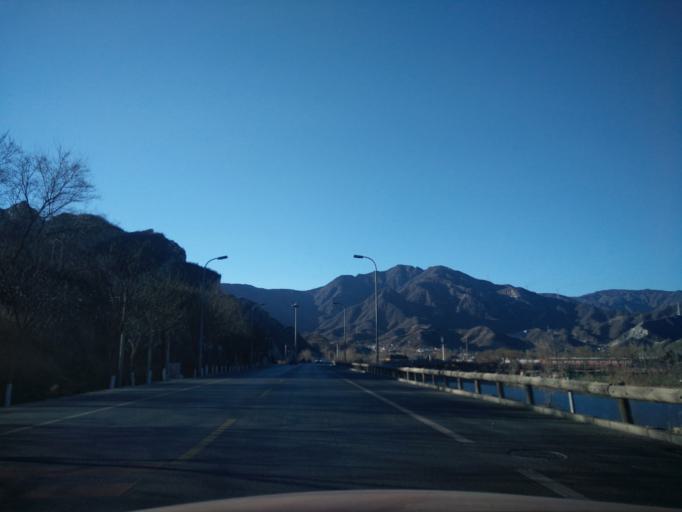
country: CN
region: Beijing
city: Miaofengshan
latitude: 39.9825
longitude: 116.0608
